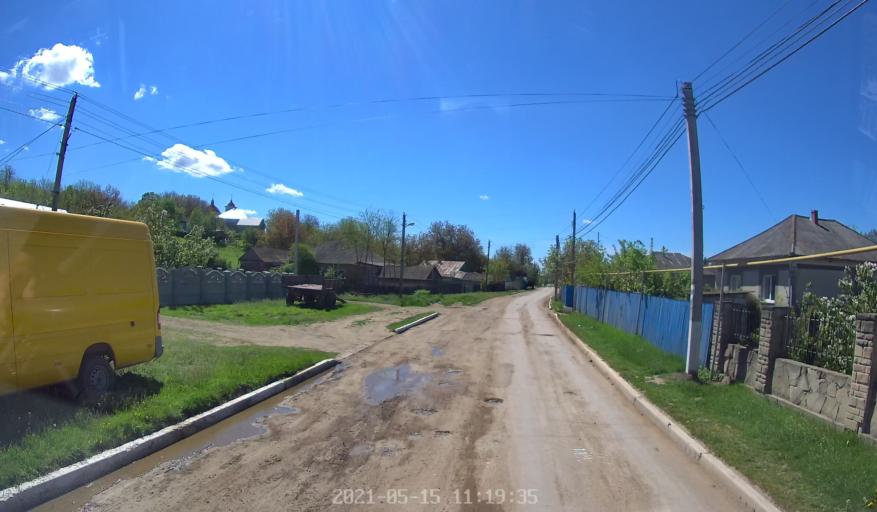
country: MD
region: Hincesti
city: Hincesti
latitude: 46.8306
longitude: 28.6765
